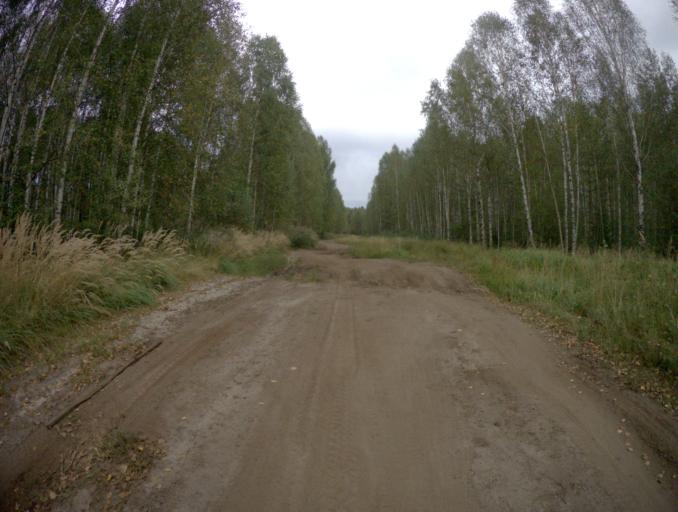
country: RU
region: Vladimir
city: Raduzhnyy
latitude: 55.9245
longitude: 40.2340
